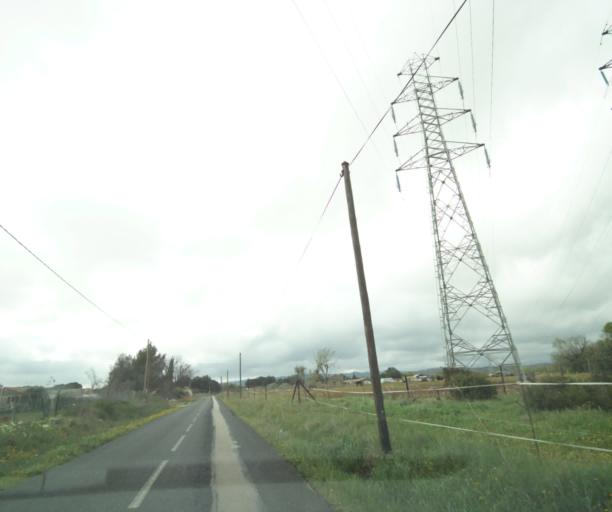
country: FR
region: Languedoc-Roussillon
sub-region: Departement de l'Herault
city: Fabregues
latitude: 43.5559
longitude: 3.7503
